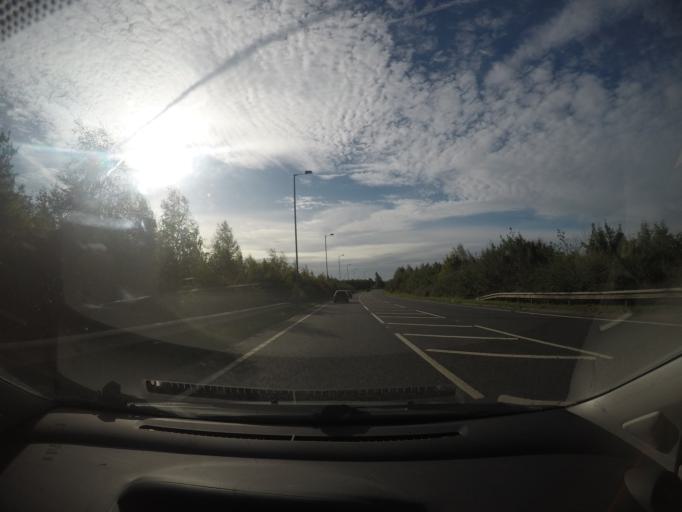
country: GB
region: England
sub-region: North Yorkshire
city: Barlby
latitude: 53.7845
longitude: -1.0368
